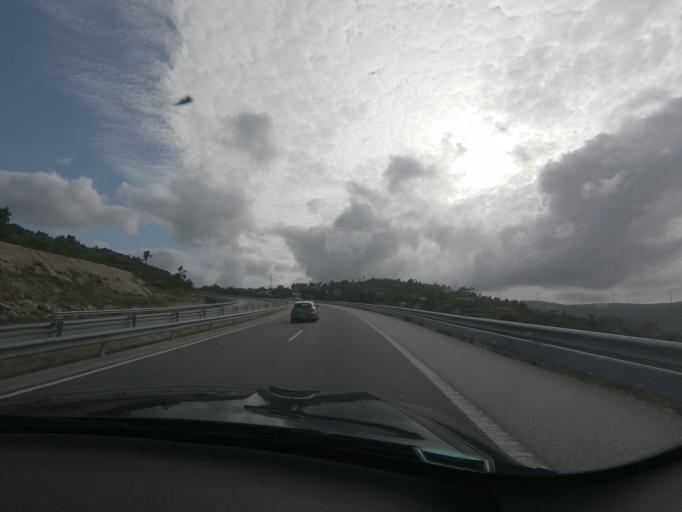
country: PT
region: Viseu
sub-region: Lamego
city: Lamego
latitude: 41.0704
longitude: -7.8281
